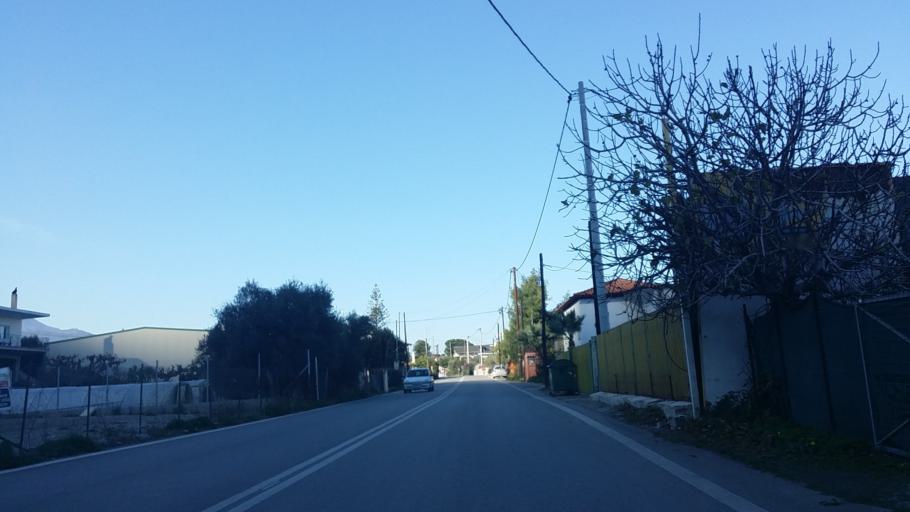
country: GR
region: West Greece
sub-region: Nomos Achaias
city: Temeni
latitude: 38.1842
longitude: 22.2009
